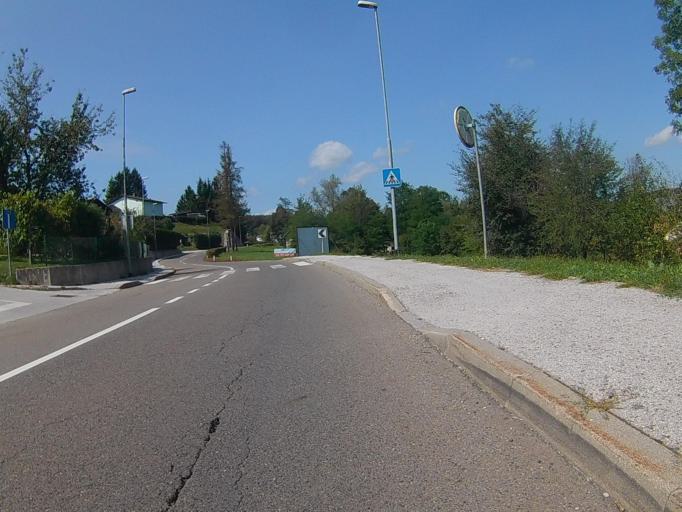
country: SI
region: Ptuj
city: Ptuj
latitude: 46.4299
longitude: 15.8610
